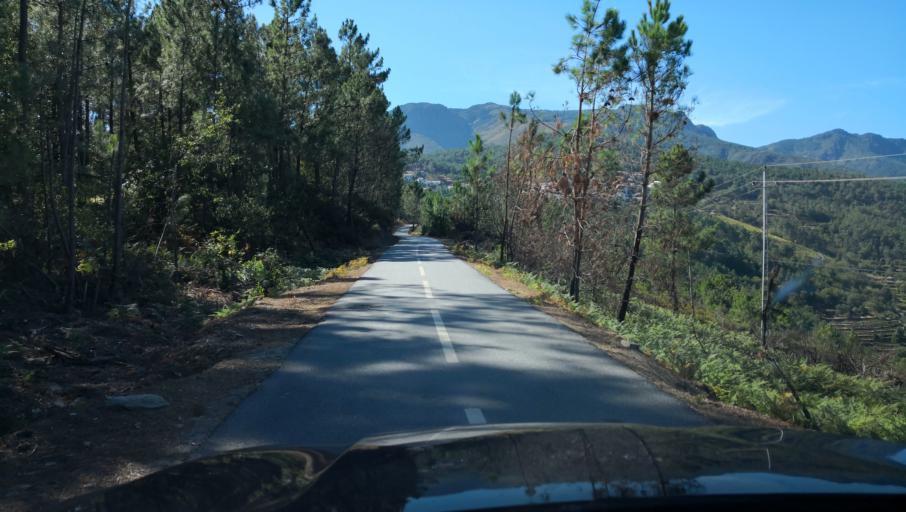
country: PT
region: Vila Real
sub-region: Santa Marta de Penaguiao
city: Santa Marta de Penaguiao
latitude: 41.2503
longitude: -7.8312
